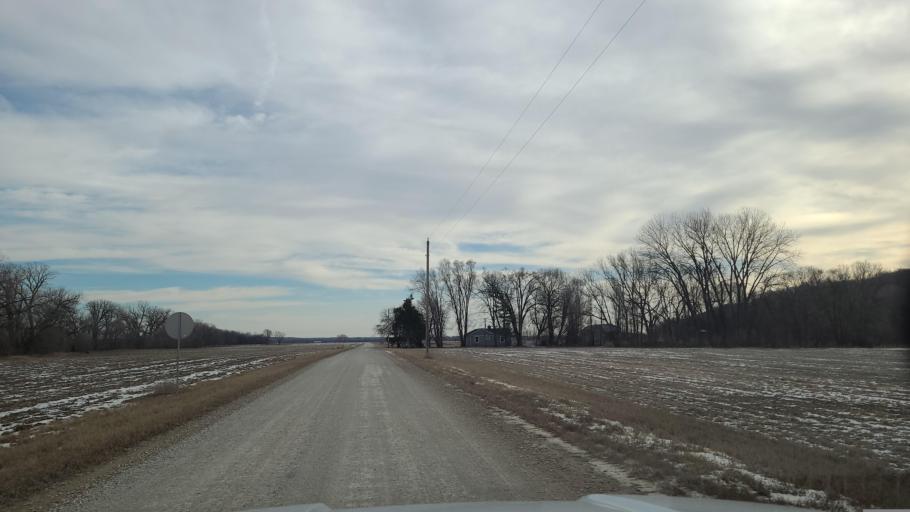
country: US
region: Kansas
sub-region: Douglas County
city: Lawrence
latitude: 39.0297
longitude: -95.3333
